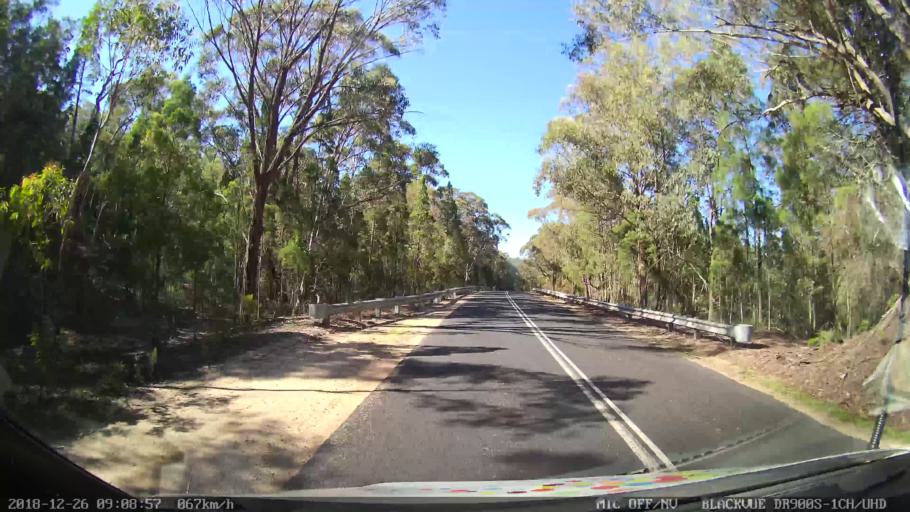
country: AU
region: New South Wales
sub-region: Mid-Western Regional
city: Kandos
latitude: -32.7202
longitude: 149.9995
